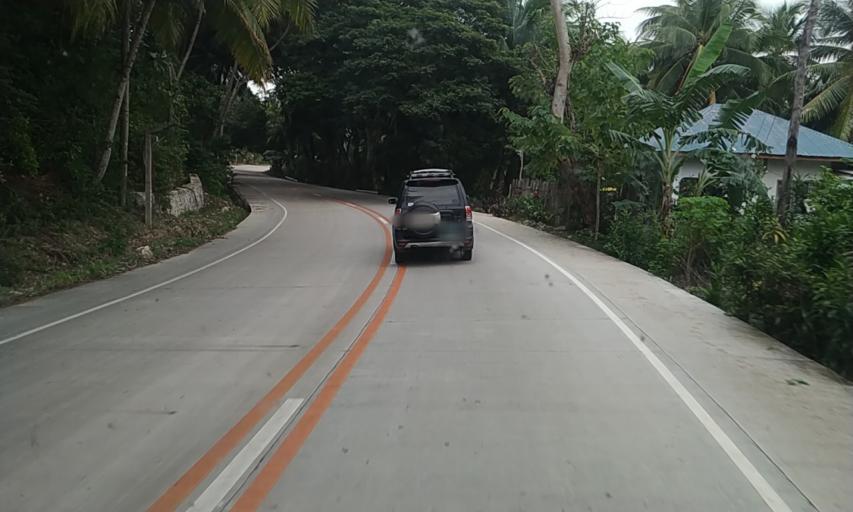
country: PH
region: Central Visayas
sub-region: Province of Negros Oriental
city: Basak
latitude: 10.2082
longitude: 123.3011
